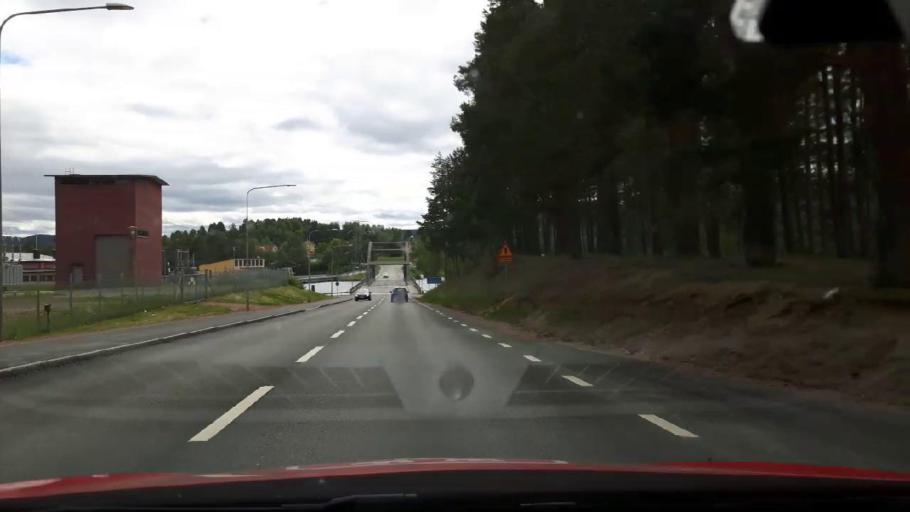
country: SE
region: Jaemtland
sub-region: Ragunda Kommun
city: Hammarstrand
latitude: 63.1153
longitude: 16.3571
